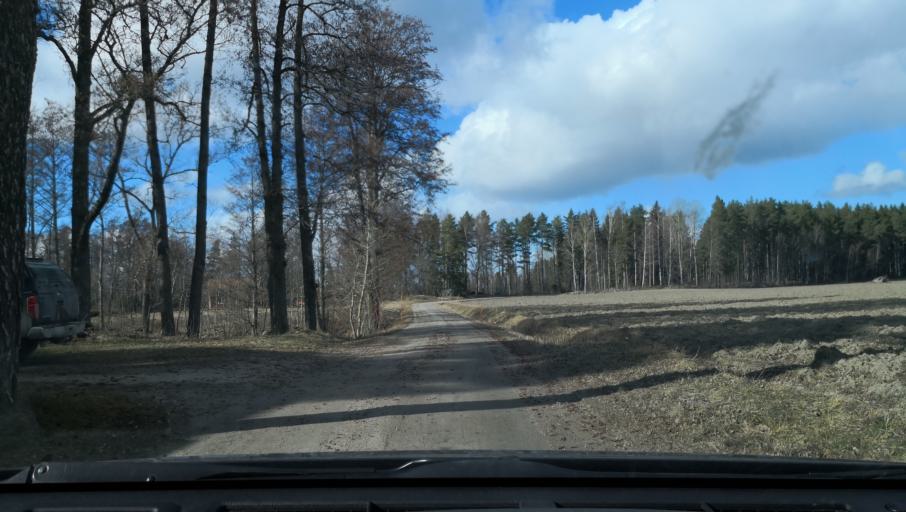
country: SE
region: OErebro
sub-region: Lindesbergs Kommun
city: Fellingsbro
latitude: 59.4261
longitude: 15.6870
